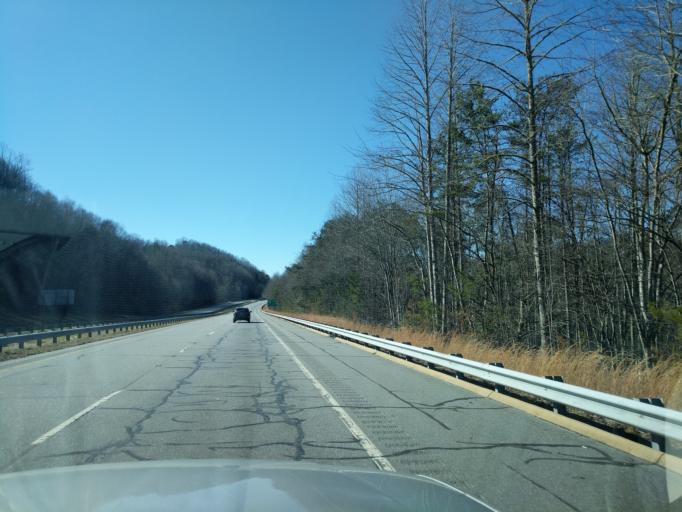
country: US
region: North Carolina
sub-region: Swain County
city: Bryson City
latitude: 35.4077
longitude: -83.4590
